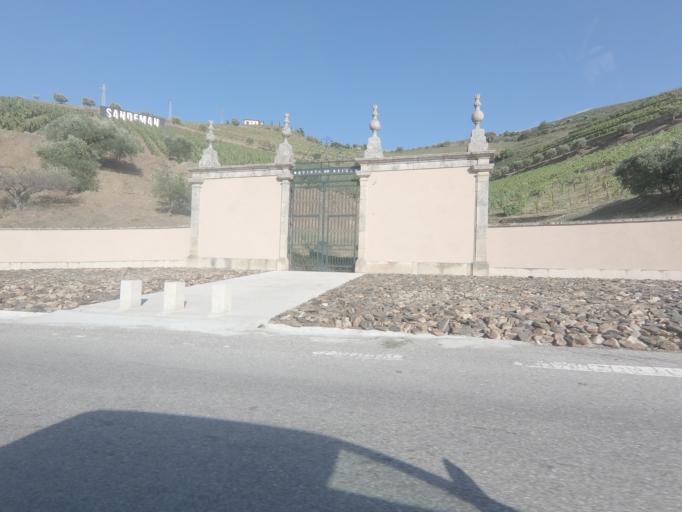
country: PT
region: Viseu
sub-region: Tabuaco
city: Tabuaco
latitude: 41.1684
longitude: -7.5594
